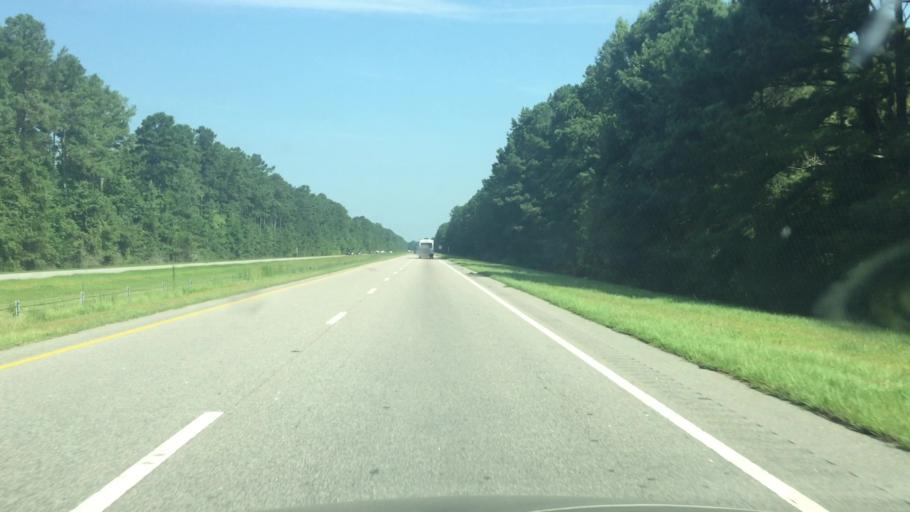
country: US
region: North Carolina
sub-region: Robeson County
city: Lumberton
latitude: 34.5450
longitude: -79.0215
